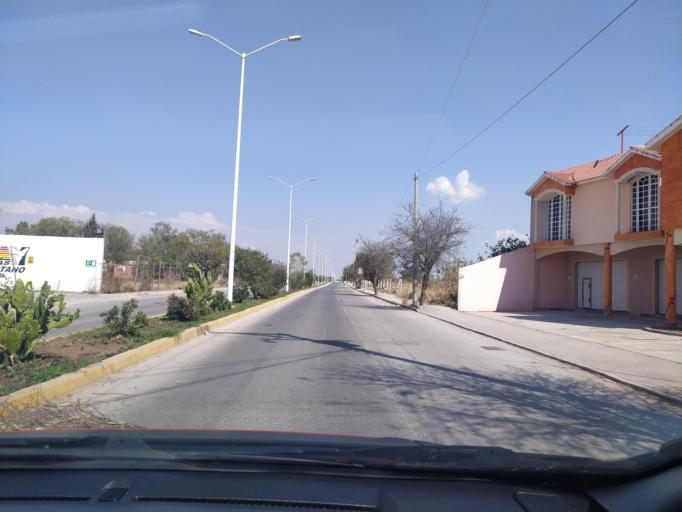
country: MX
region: Guanajuato
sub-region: San Francisco del Rincon
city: Fraccionamiento la Mezquitera
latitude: 21.0175
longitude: -101.8405
